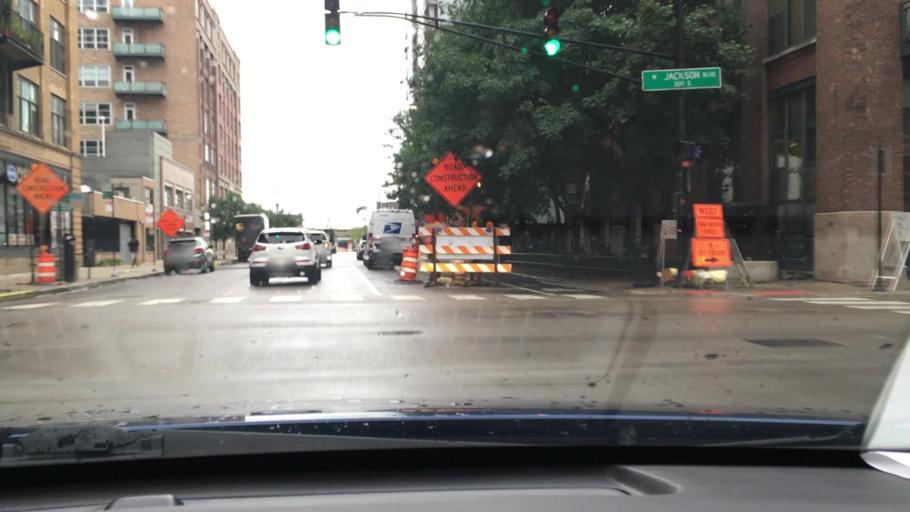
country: US
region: Illinois
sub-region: Cook County
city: Chicago
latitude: 41.8781
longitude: -87.6440
